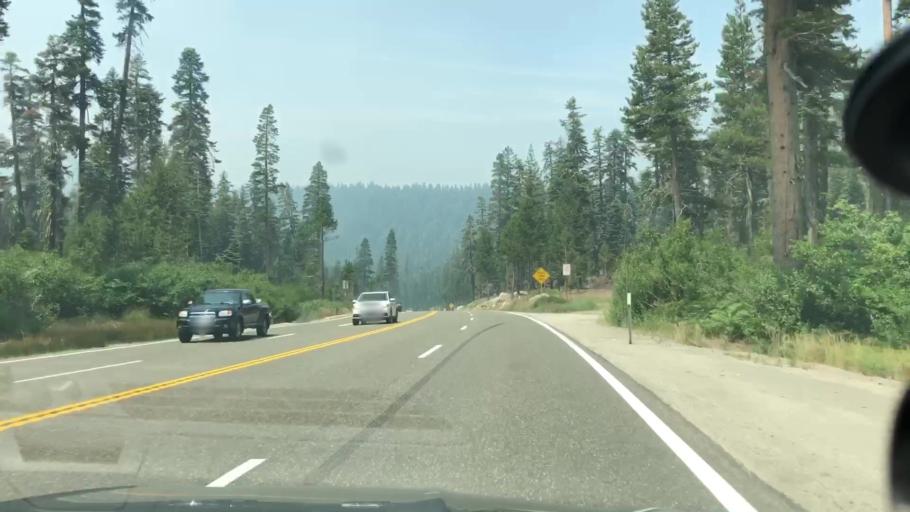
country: US
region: California
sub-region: El Dorado County
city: South Lake Tahoe
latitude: 38.8188
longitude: -120.0350
